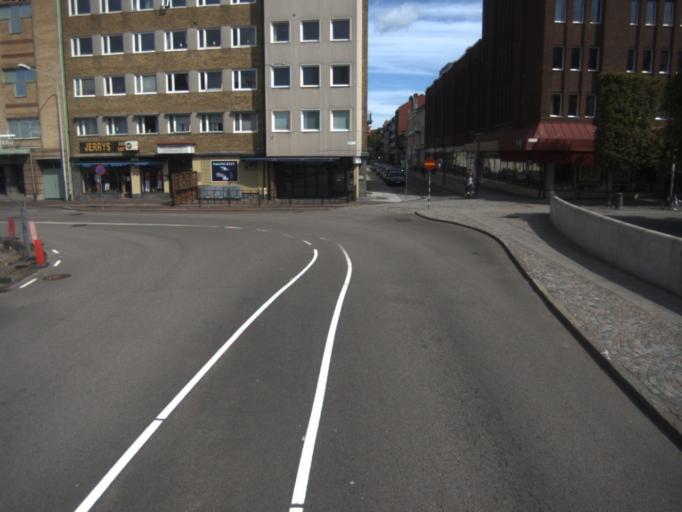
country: SE
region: Skane
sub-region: Helsingborg
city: Helsingborg
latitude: 56.0407
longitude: 12.7004
